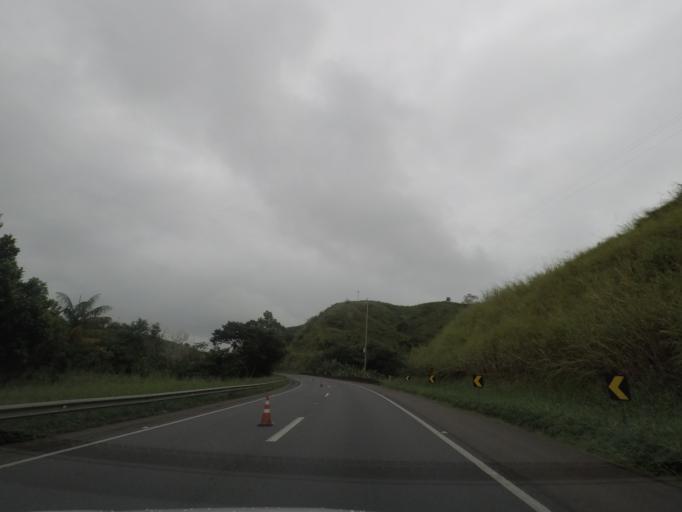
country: BR
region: Sao Paulo
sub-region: Cajati
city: Cajati
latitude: -24.8024
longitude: -48.2110
